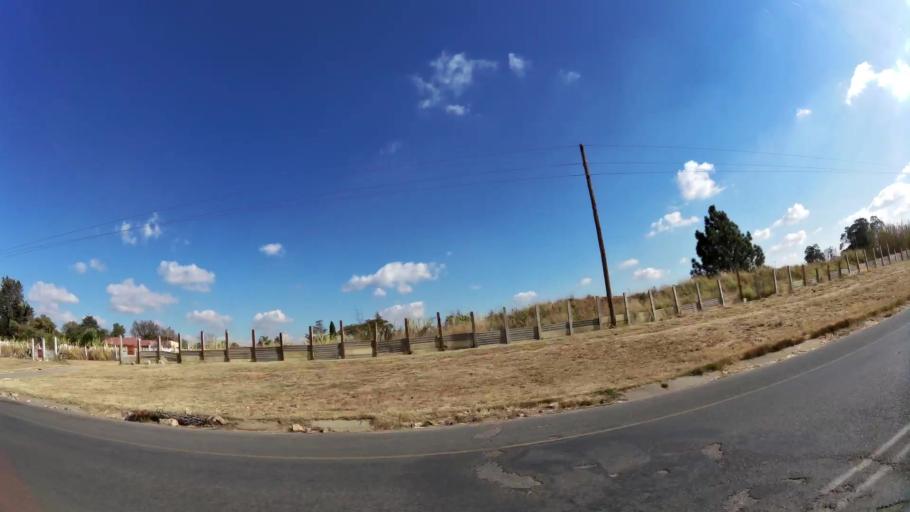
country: ZA
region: Gauteng
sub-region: West Rand District Municipality
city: Muldersdriseloop
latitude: -26.0477
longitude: 27.9067
